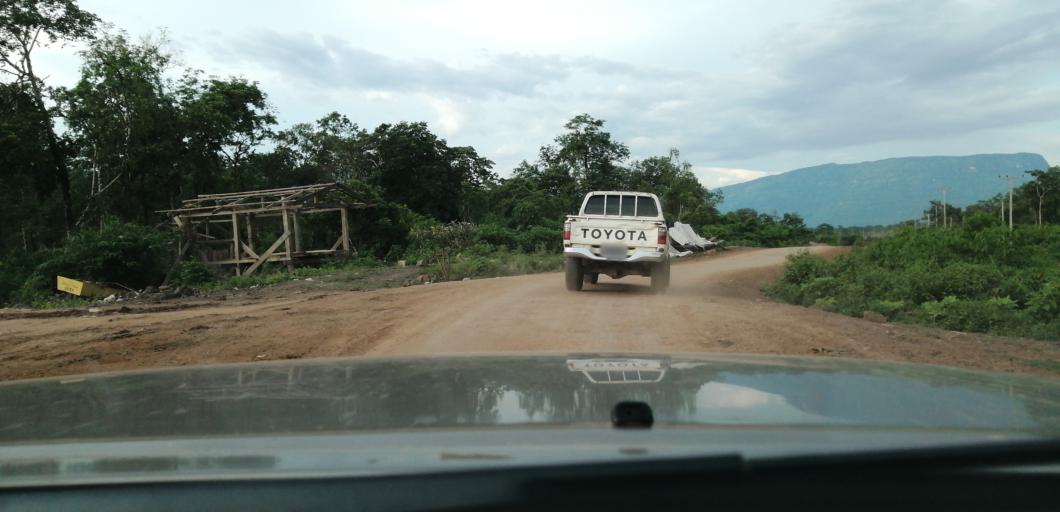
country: LA
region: Attapu
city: Attapu
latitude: 14.7087
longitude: 106.4778
